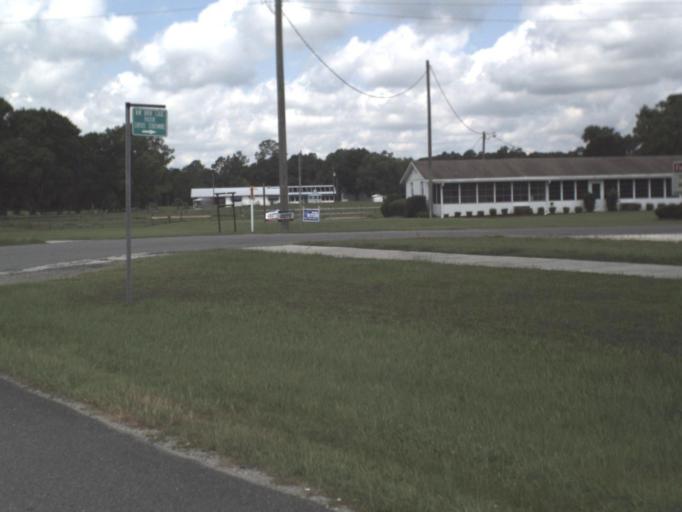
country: US
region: Florida
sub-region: Union County
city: Lake Butler
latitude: 30.0639
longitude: -82.2364
